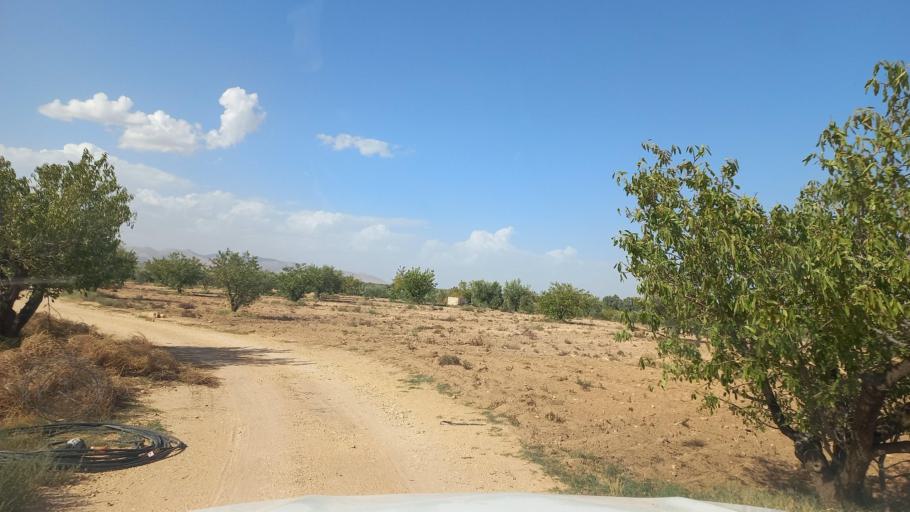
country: TN
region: Al Qasrayn
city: Sbiba
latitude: 35.3020
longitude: 9.0421
